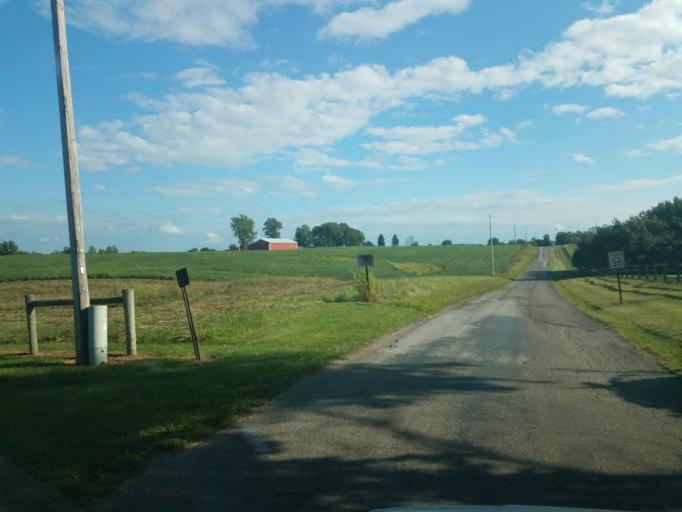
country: US
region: Ohio
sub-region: Knox County
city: Fredericktown
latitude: 40.4148
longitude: -82.5629
